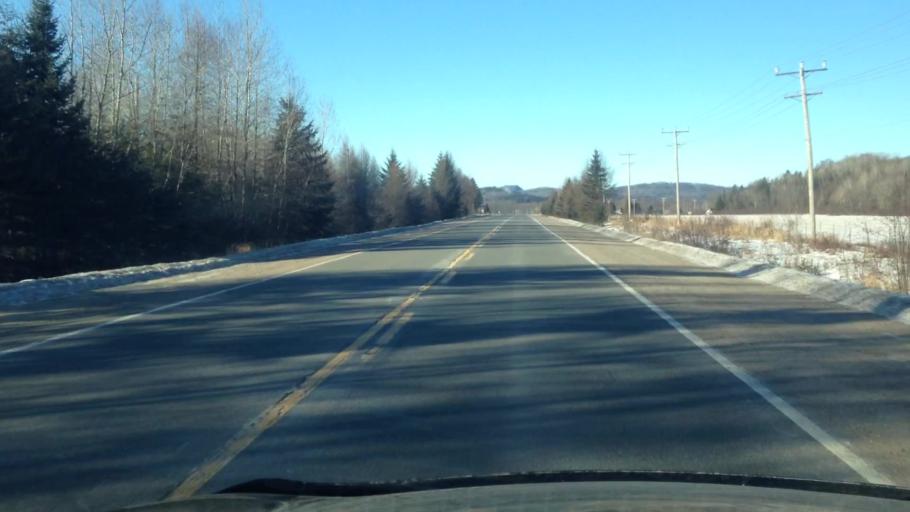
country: CA
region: Quebec
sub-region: Laurentides
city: Mont-Tremblant
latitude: 46.0551
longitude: -74.6166
